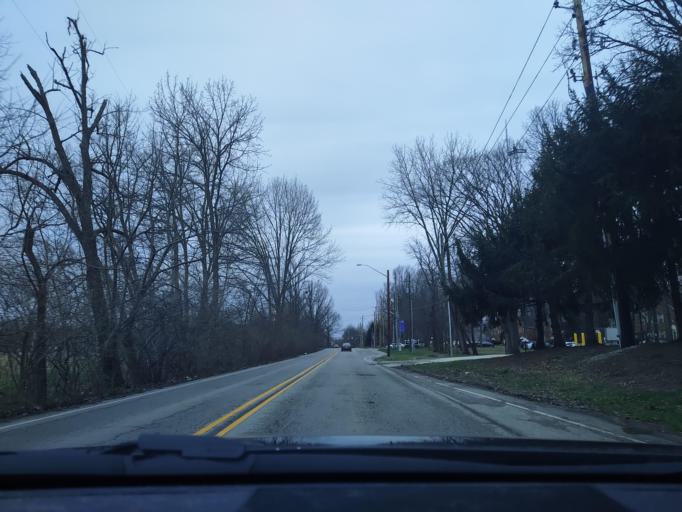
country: US
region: Indiana
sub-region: Marion County
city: Meridian Hills
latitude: 39.9001
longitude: -86.2031
